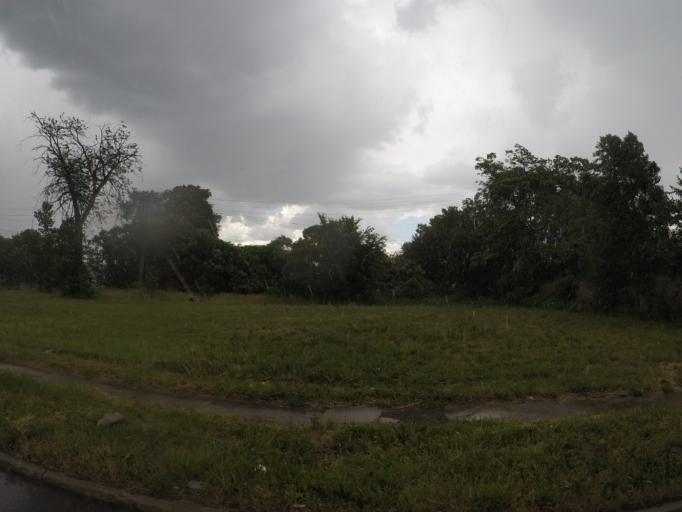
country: US
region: Michigan
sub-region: Wayne County
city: River Rouge
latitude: 42.3207
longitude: -83.1126
